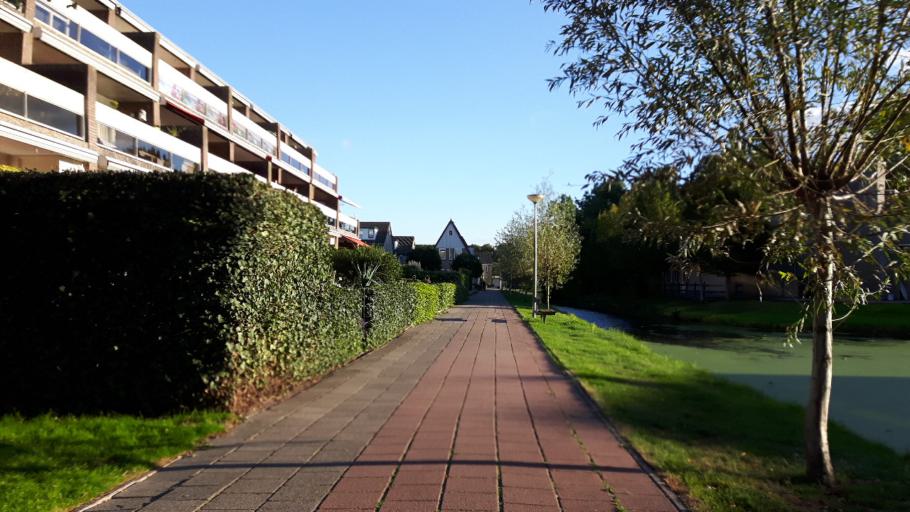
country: NL
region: Utrecht
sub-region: Gemeente Oudewater
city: Oudewater
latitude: 52.0284
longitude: 4.8709
